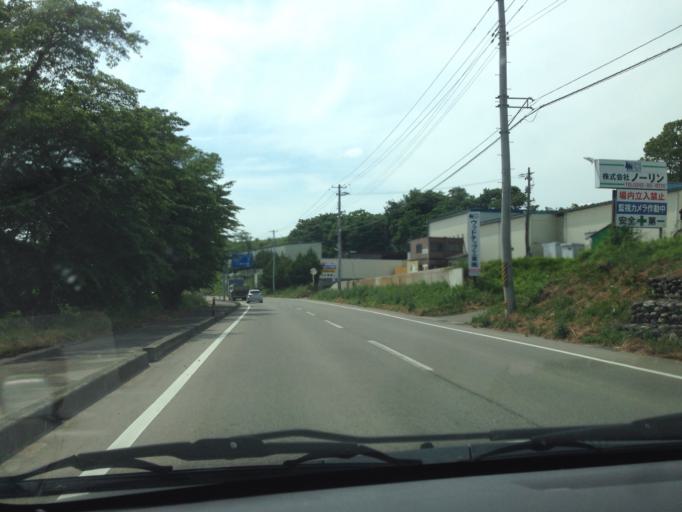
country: JP
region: Fukushima
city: Kitakata
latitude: 37.6134
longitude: 139.8076
